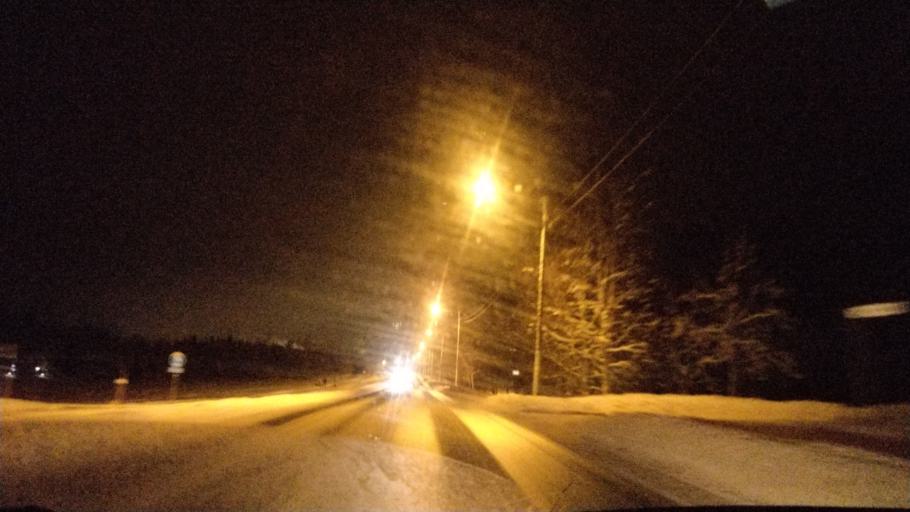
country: FI
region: Lapland
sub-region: Rovaniemi
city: Rovaniemi
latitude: 66.3912
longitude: 25.3791
